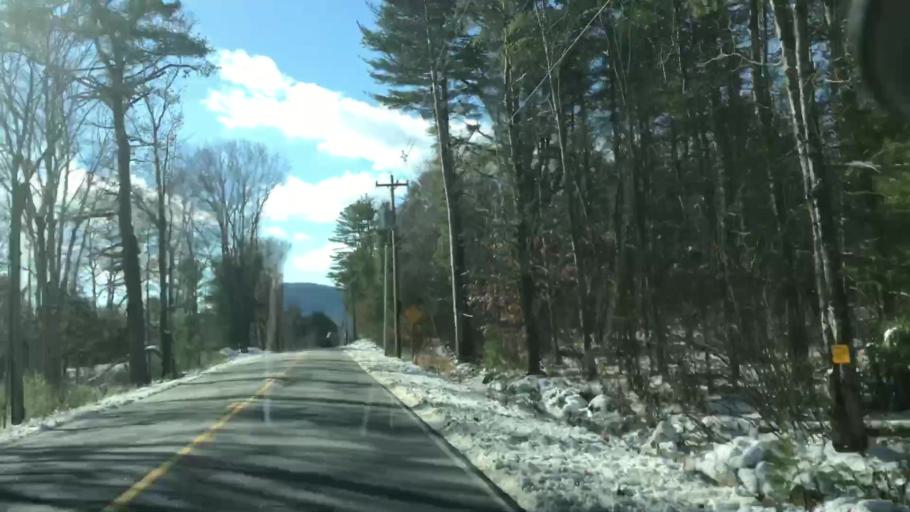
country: US
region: Maine
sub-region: Oxford County
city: Brownfield
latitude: 43.9591
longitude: -70.8799
